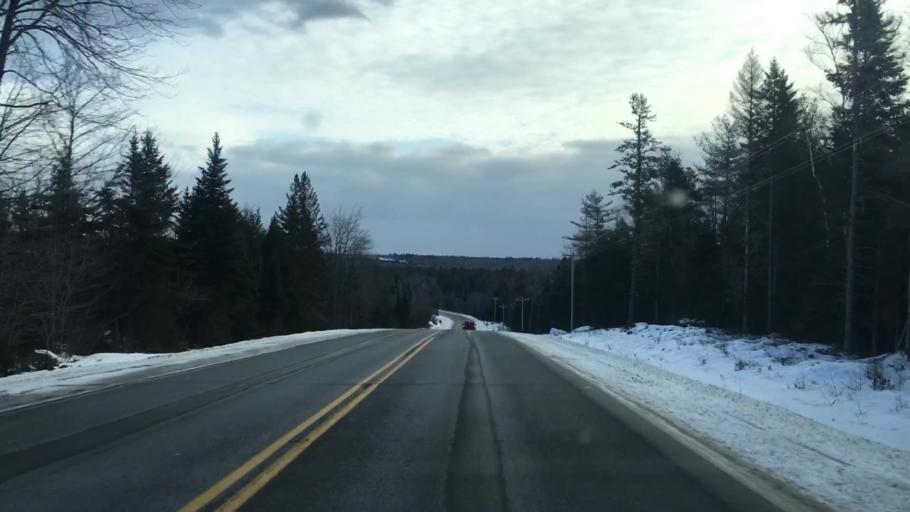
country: US
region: Maine
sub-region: Washington County
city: Machias
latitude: 44.9994
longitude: -67.5916
